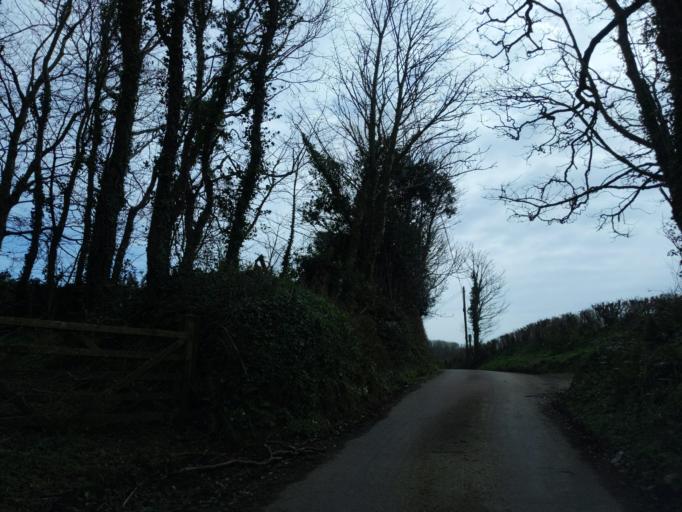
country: GB
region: England
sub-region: Devon
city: Yealmpton
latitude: 50.3625
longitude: -4.0045
